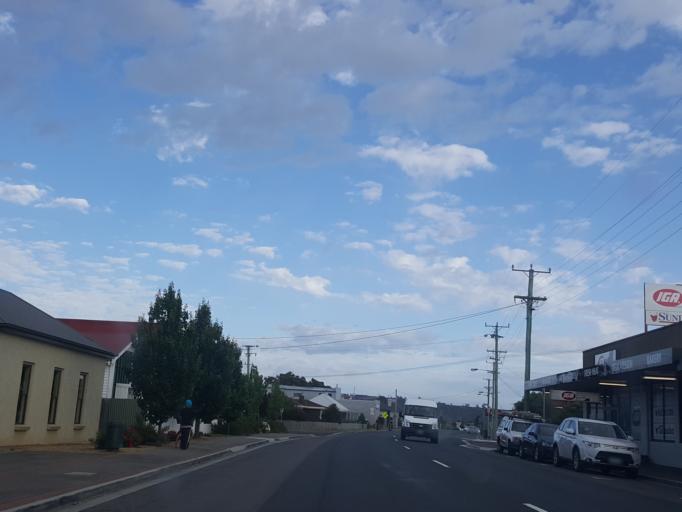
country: AU
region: Tasmania
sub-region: Northern Midlands
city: Perth
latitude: -41.5771
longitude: 147.1748
